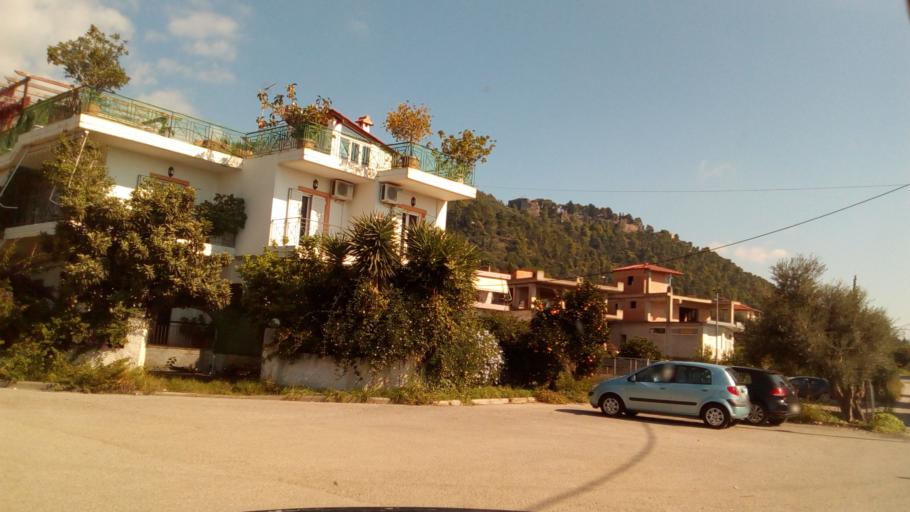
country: GR
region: West Greece
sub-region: Nomos Aitolias kai Akarnanias
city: Nafpaktos
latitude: 38.3925
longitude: 21.8158
